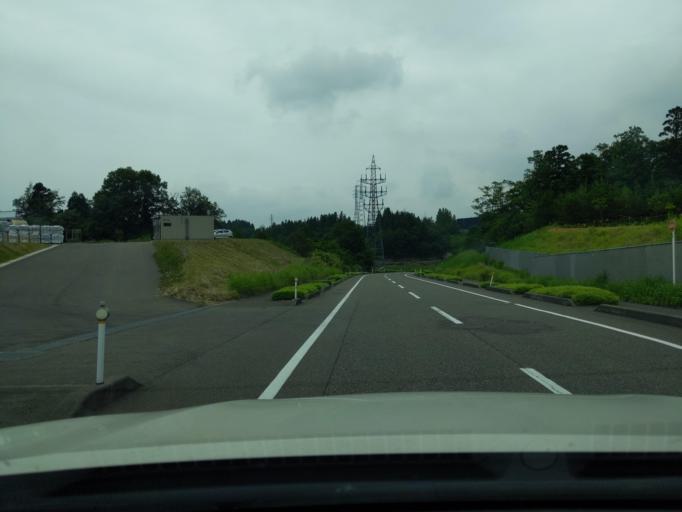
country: JP
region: Niigata
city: Kashiwazaki
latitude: 37.3404
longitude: 138.5916
